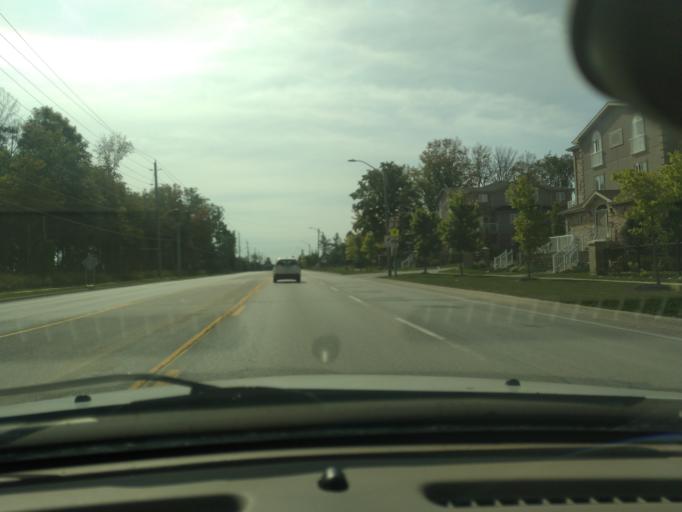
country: CA
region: Ontario
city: Barrie
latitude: 44.3445
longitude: -79.7019
